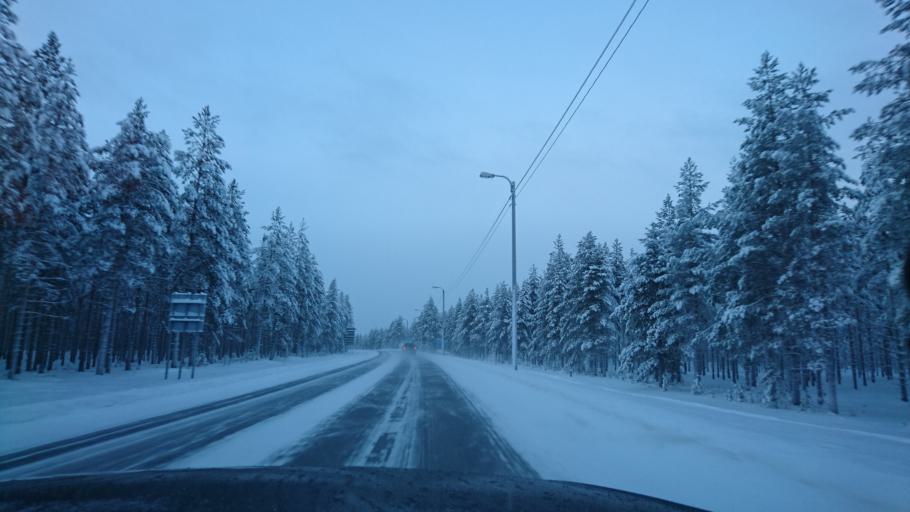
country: FI
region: Kainuu
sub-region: Kehys-Kainuu
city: Puolanka
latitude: 65.4299
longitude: 27.5318
